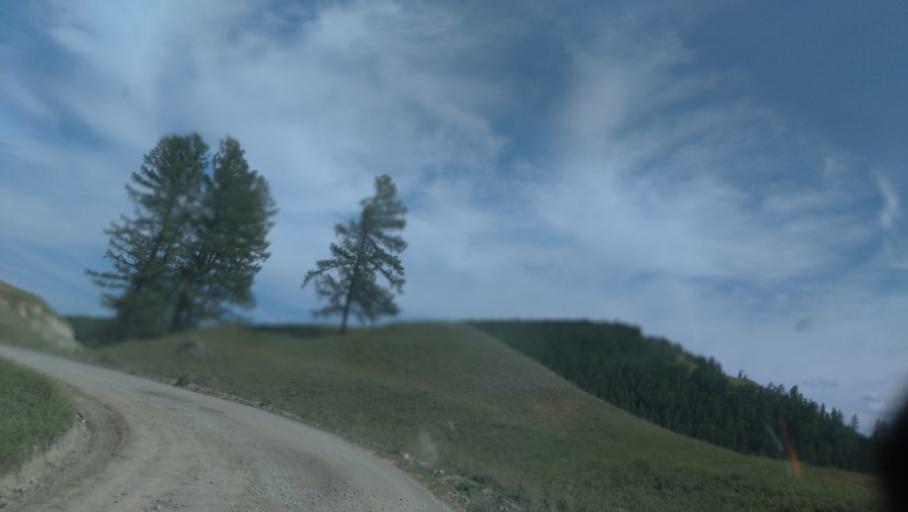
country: RU
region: Altay
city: Ust'-Ulagan
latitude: 50.7707
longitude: 88.1716
